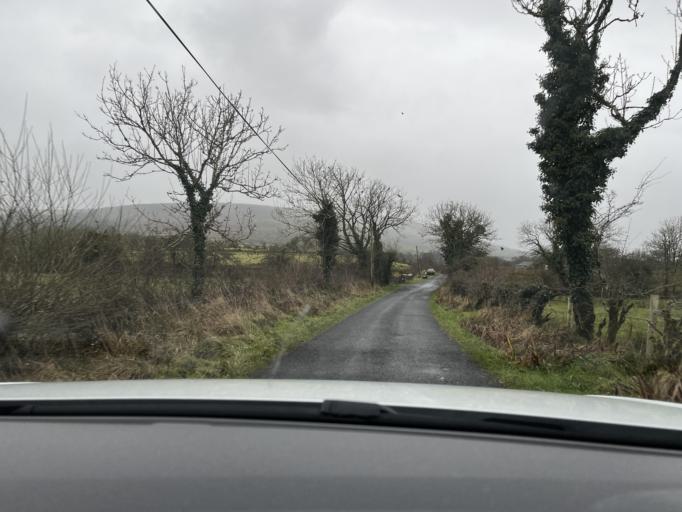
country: IE
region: Connaught
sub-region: County Leitrim
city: Manorhamilton
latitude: 54.2928
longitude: -8.0827
